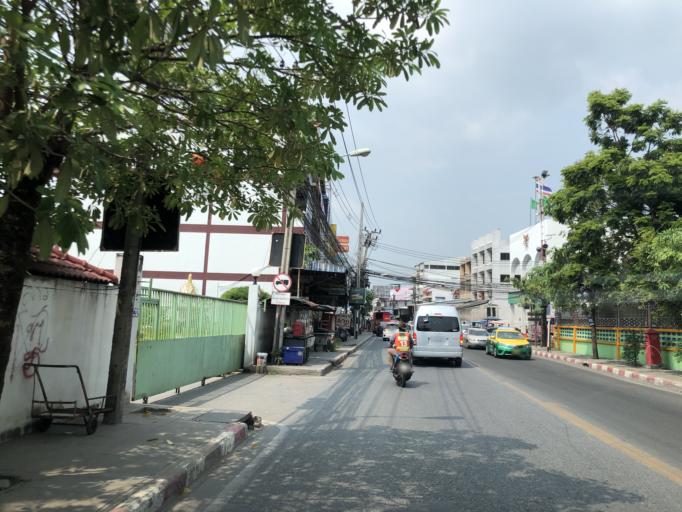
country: TH
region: Samut Prakan
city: Bang Bo
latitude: 13.5718
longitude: 100.8373
